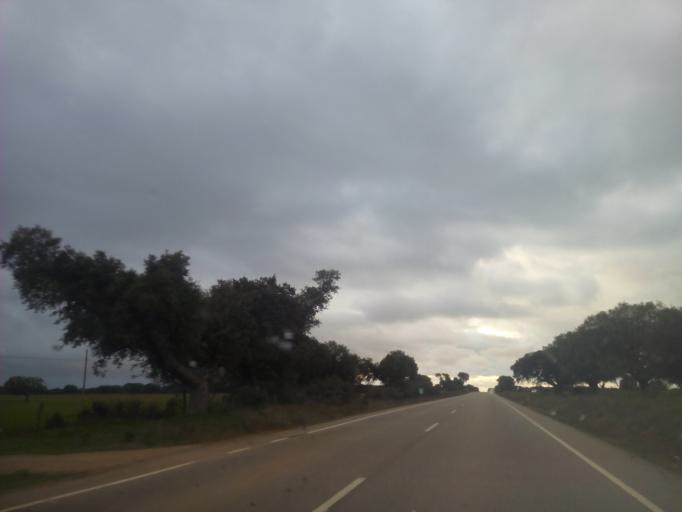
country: ES
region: Castille and Leon
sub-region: Provincia de Salamanca
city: Cabrillas
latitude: 40.7573
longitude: -6.1932
